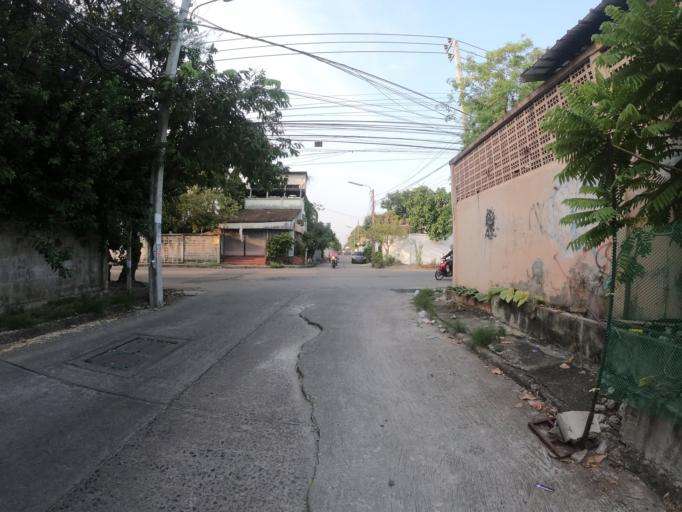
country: TH
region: Bangkok
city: Lat Phrao
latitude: 13.8252
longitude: 100.6081
